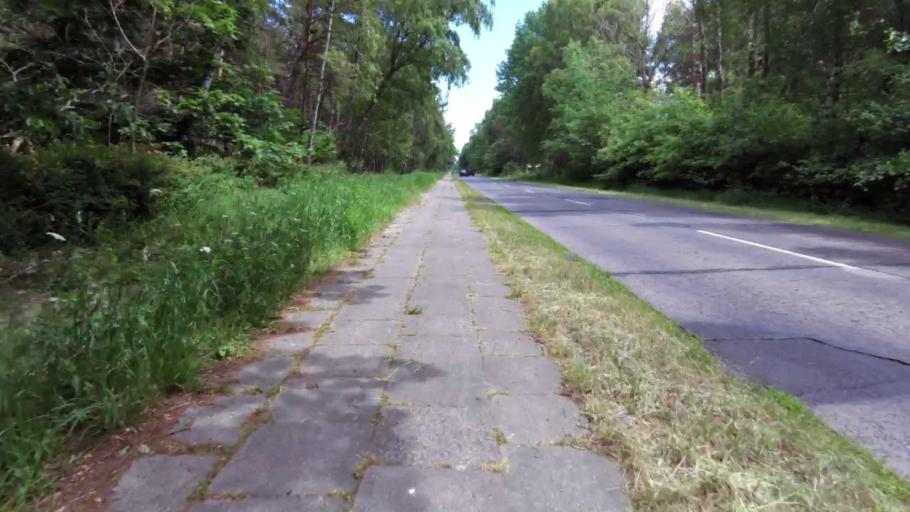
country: PL
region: West Pomeranian Voivodeship
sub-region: Powiat kamienski
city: Dziwnow
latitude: 54.0115
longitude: 14.7193
